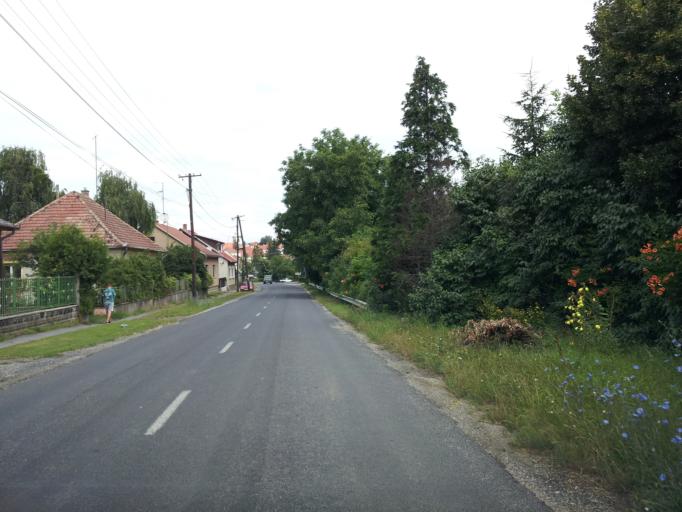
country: HU
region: Vas
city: Vasvar
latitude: 47.0449
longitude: 16.7973
